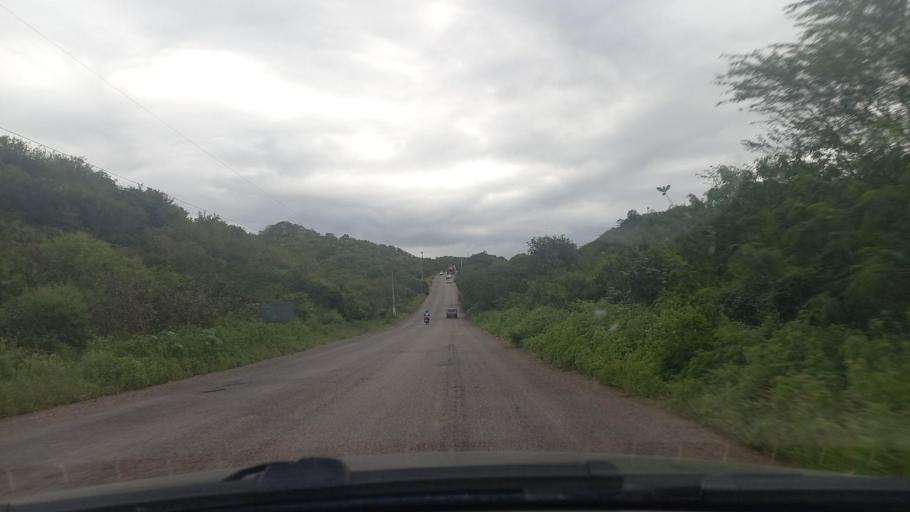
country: BR
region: Sergipe
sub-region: Caninde De Sao Francisco
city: Caninde de Sao Francisco
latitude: -9.6326
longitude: -37.7779
